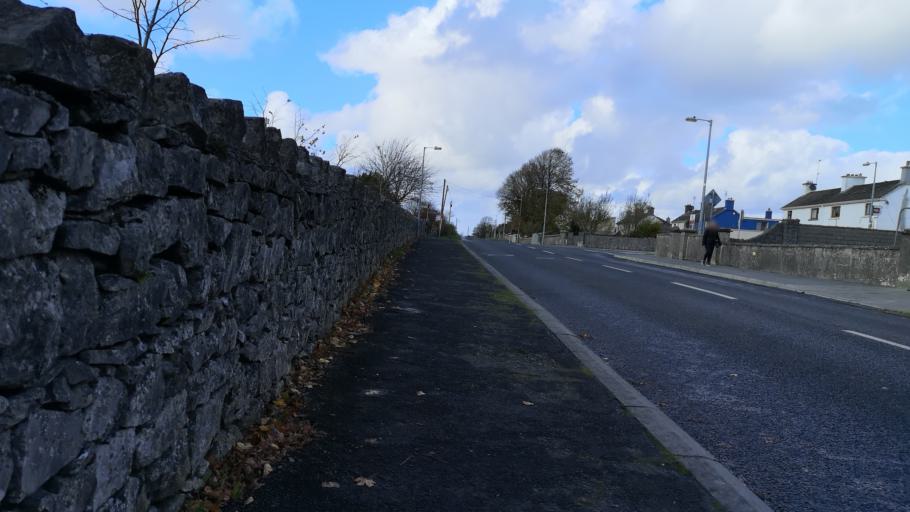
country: IE
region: Connaught
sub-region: County Galway
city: Athenry
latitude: 53.3043
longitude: -8.7502
